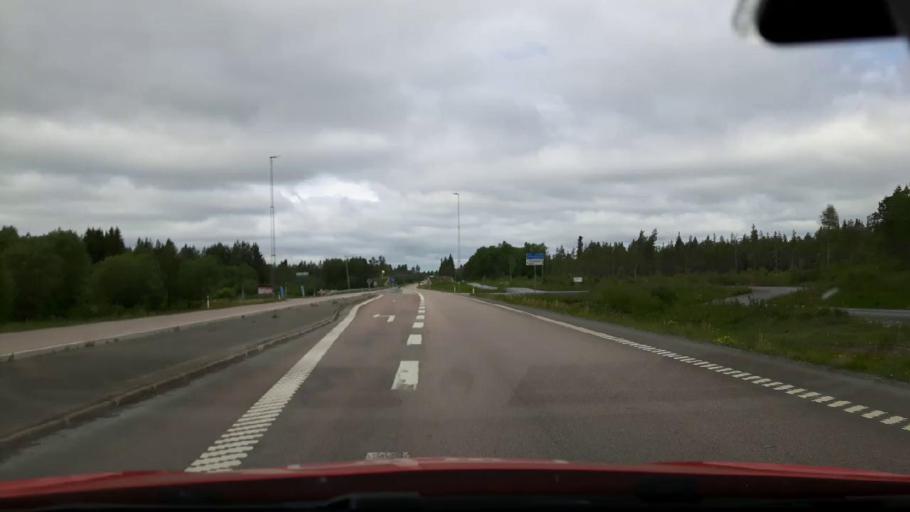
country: SE
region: Jaemtland
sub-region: Krokoms Kommun
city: Krokom
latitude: 63.2859
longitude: 14.5145
